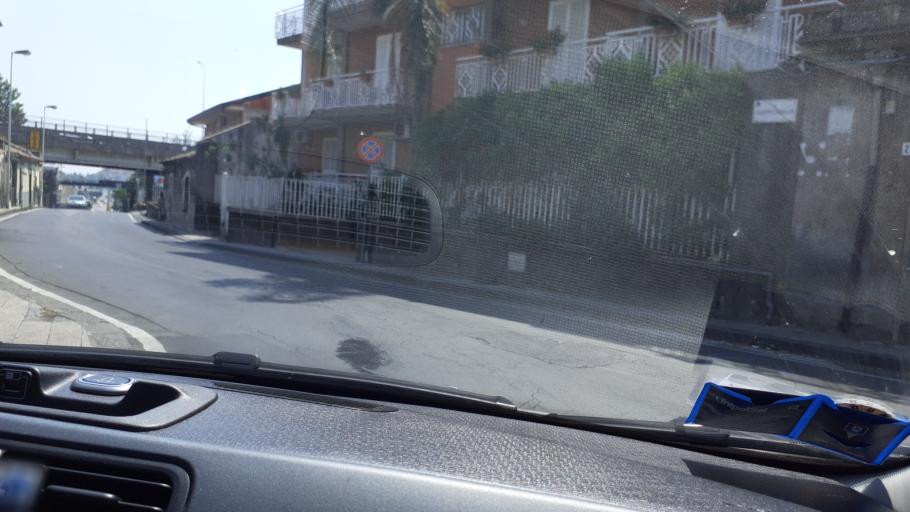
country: IT
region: Sicily
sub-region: Catania
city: Misterbianco
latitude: 37.5164
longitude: 15.0189
